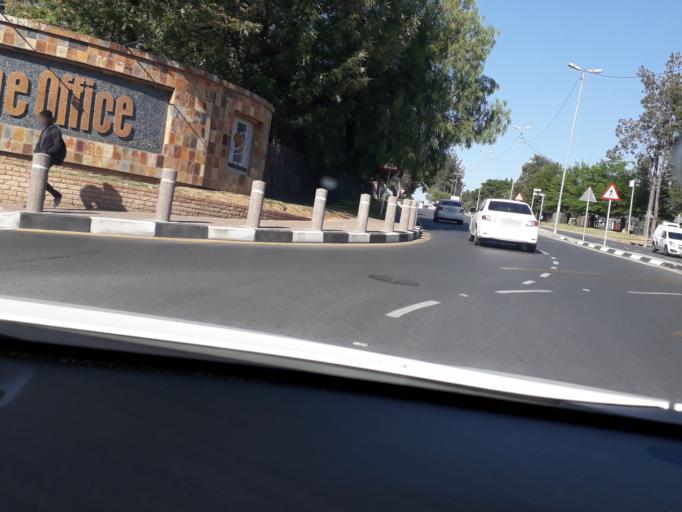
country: ZA
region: Gauteng
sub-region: City of Johannesburg Metropolitan Municipality
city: Diepsloot
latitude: -26.0409
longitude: 28.0200
